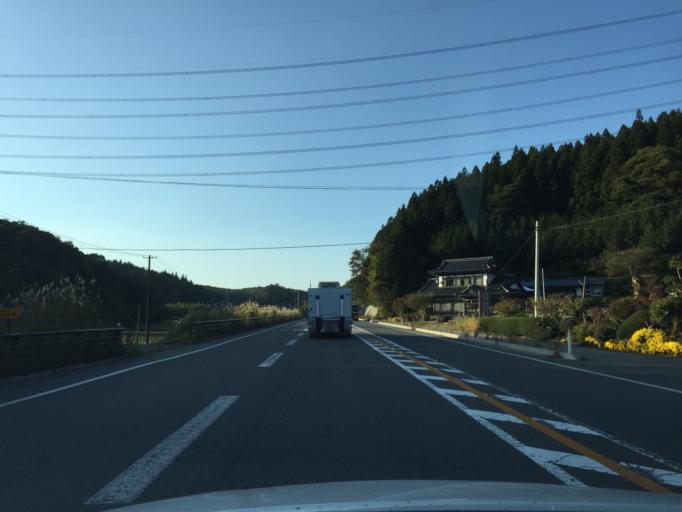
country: JP
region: Fukushima
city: Ishikawa
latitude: 37.1936
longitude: 140.6201
